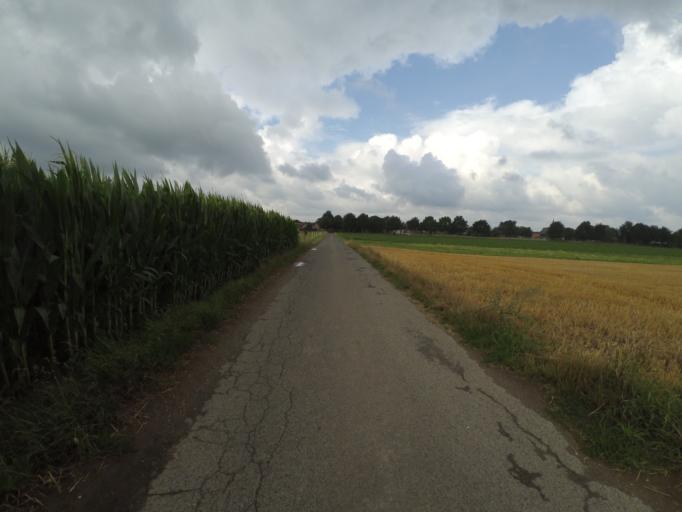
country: DE
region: North Rhine-Westphalia
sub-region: Regierungsbezirk Koln
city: Gangelt
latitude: 51.0052
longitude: 5.9772
